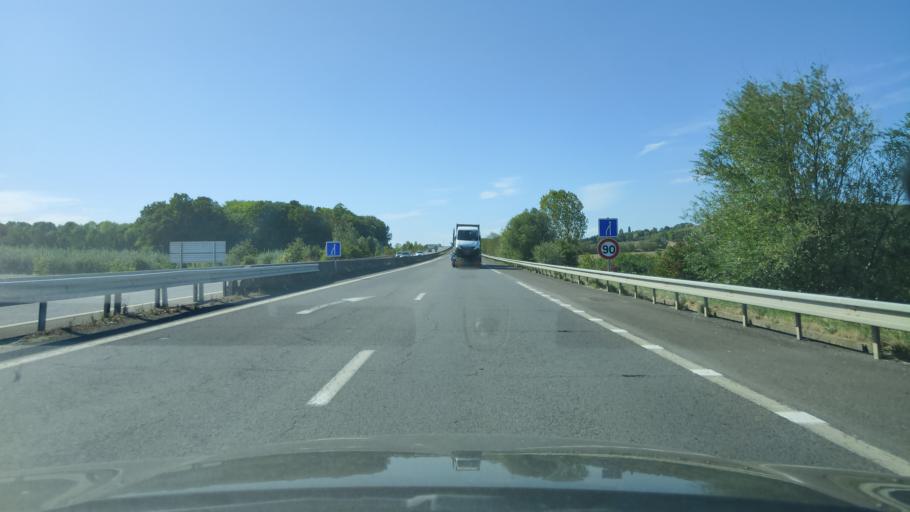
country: FR
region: Lorraine
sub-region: Departement de la Moselle
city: Augny
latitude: 49.0376
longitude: 6.1221
